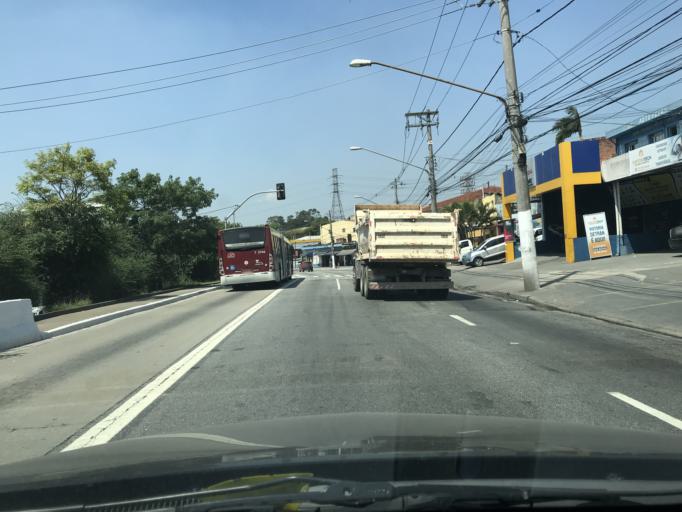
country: BR
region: Sao Paulo
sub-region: Taboao Da Serra
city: Taboao da Serra
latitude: -23.6679
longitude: -46.7313
